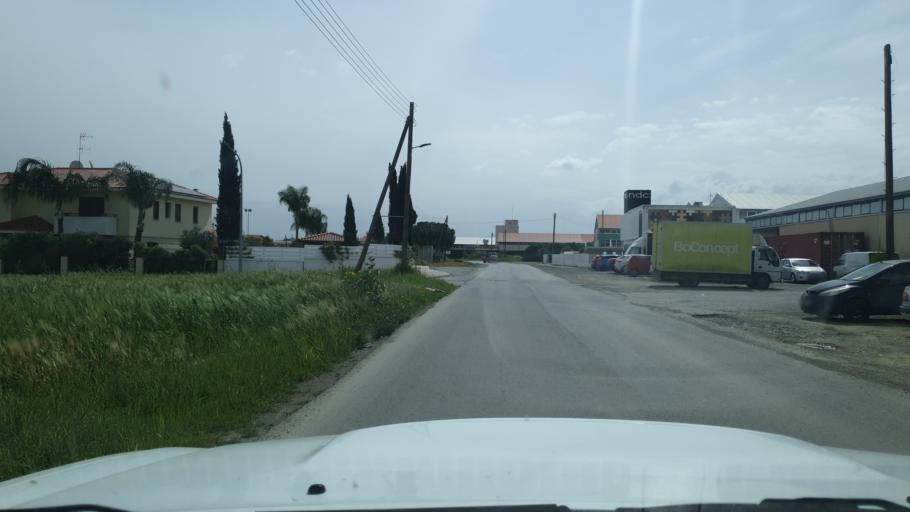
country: CY
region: Lefkosia
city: Geri
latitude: 35.0897
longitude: 33.3846
